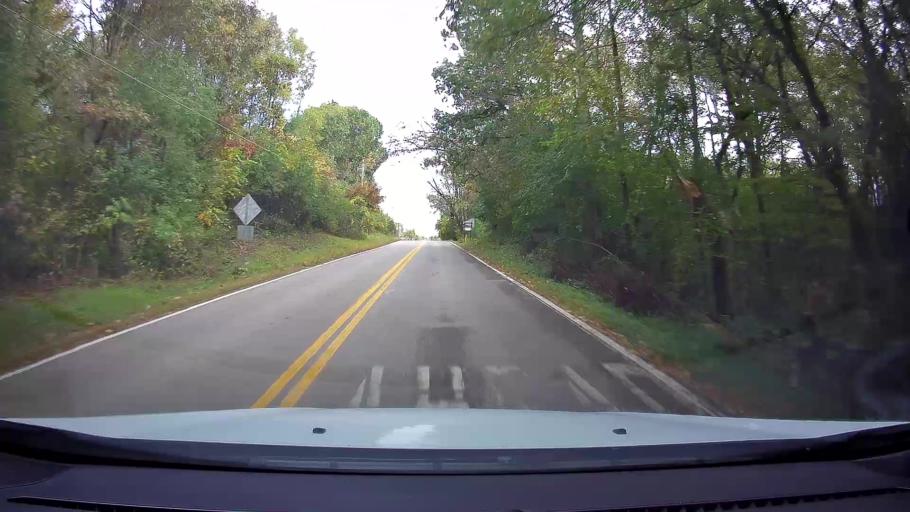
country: US
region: Minnesota
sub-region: Washington County
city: Stillwater
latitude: 45.1093
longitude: -92.7841
